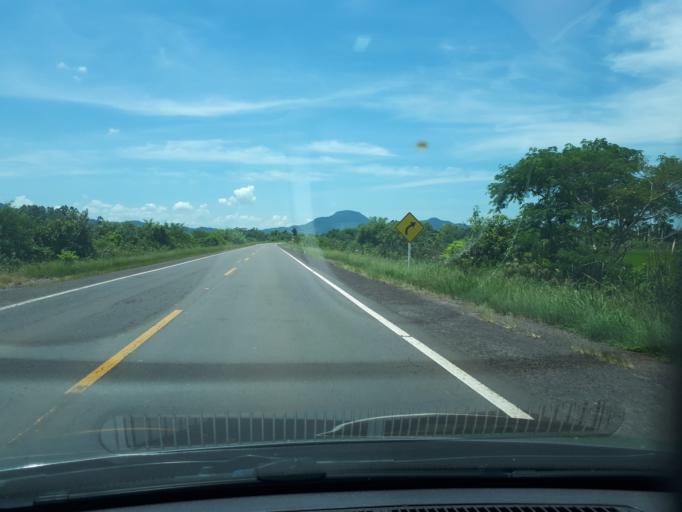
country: BR
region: Rio Grande do Sul
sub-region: Candelaria
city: Candelaria
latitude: -29.7260
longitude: -52.9311
